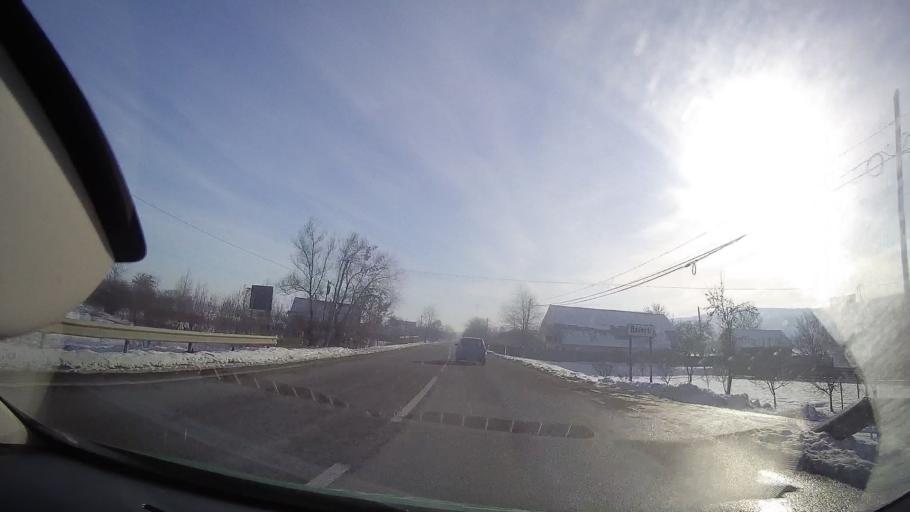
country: RO
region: Neamt
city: Bodesti
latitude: 47.0465
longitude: 26.4044
